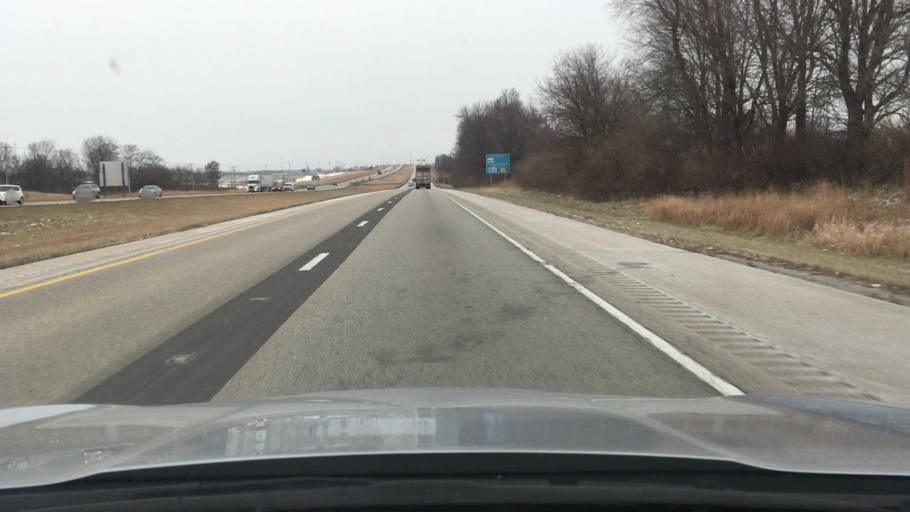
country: US
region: Illinois
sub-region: Sangamon County
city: Divernon
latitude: 39.5765
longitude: -89.6461
